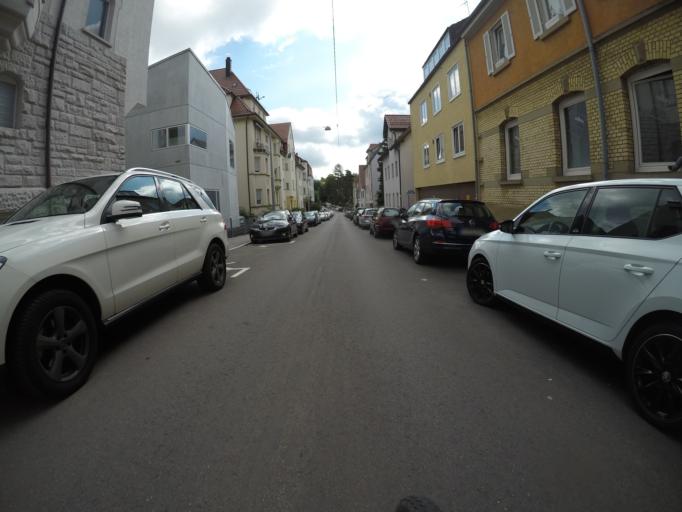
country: DE
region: Baden-Wuerttemberg
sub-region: Regierungsbezirk Stuttgart
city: Stuttgart
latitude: 48.7479
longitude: 9.1734
